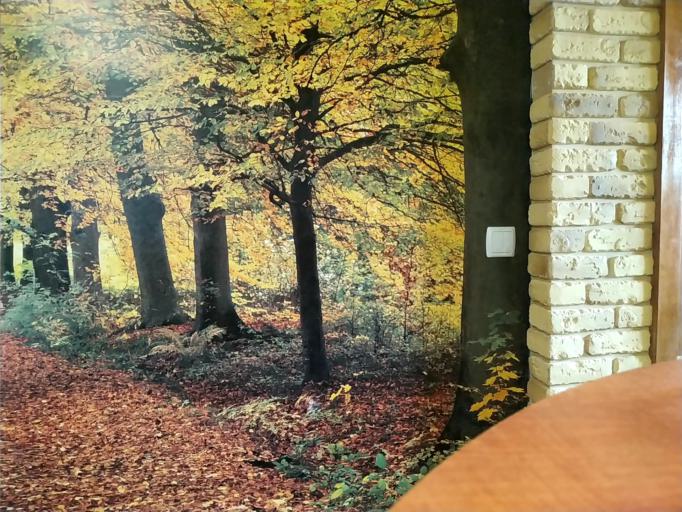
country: RU
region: Novgorod
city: Opechenskiy Posad
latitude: 58.2661
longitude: 34.0317
